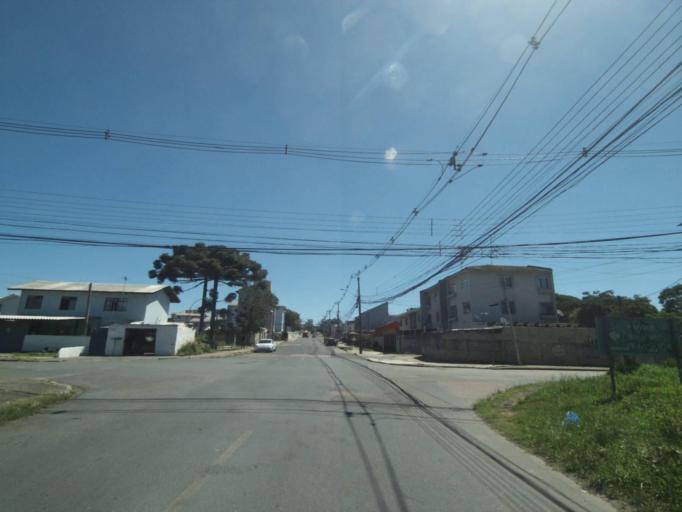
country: BR
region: Parana
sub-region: Curitiba
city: Curitiba
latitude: -25.4718
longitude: -49.3467
